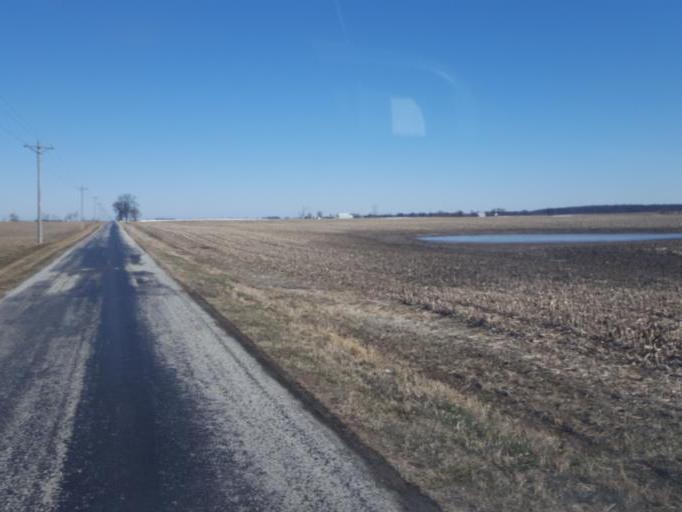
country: US
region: Ohio
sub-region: Marion County
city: Marion
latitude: 40.6476
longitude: -83.1979
